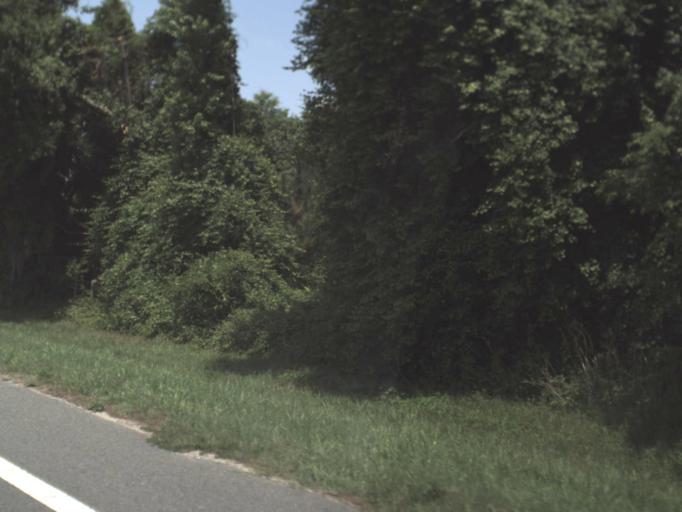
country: US
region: Florida
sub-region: Levy County
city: Williston
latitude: 29.4954
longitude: -82.4066
